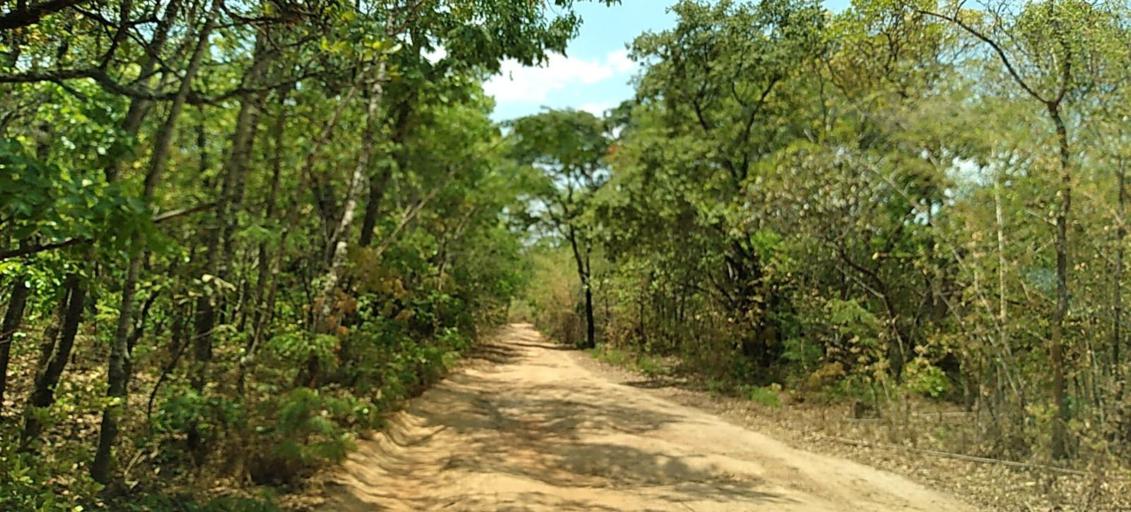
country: ZM
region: Copperbelt
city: Chililabombwe
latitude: -12.4891
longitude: 27.6385
